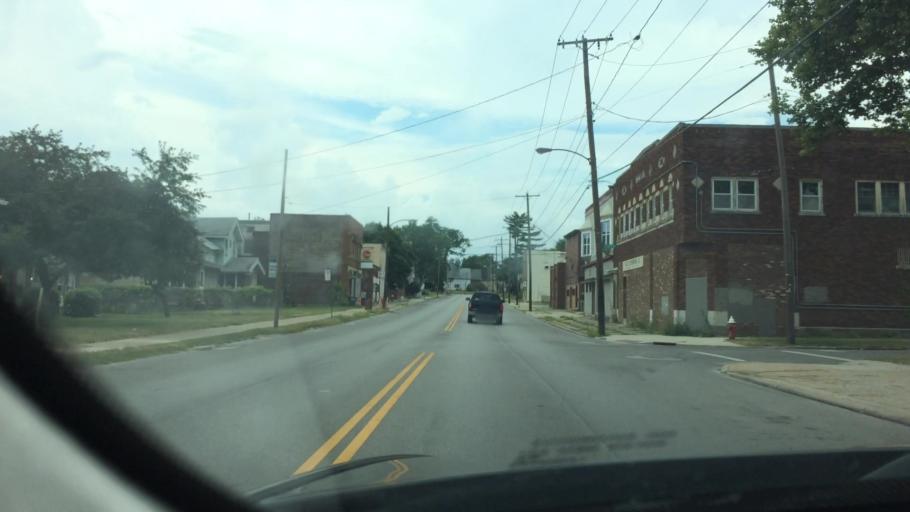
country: US
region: Ohio
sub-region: Wood County
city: Rossford
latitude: 41.6349
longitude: -83.5781
